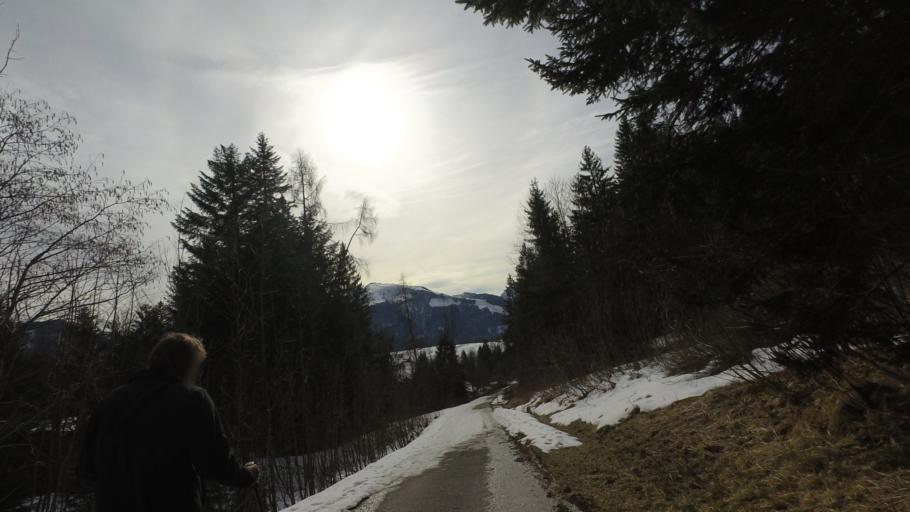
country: DE
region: Bavaria
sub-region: Upper Bavaria
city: Reit im Winkl
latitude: 47.6822
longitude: 12.4482
